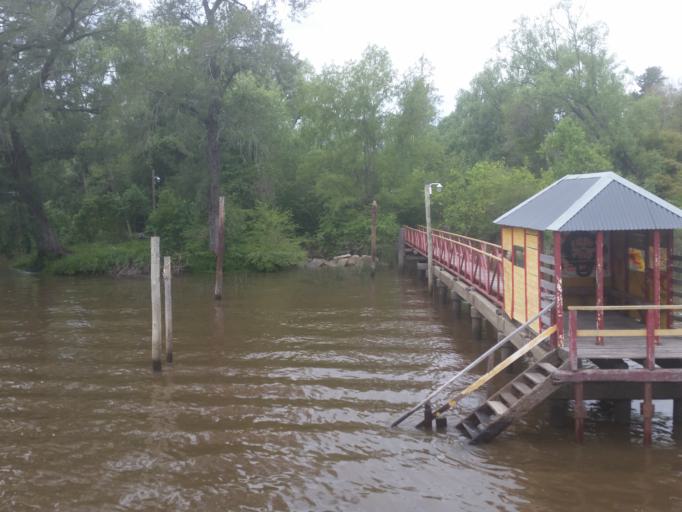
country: AR
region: Buenos Aires
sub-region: Partido de Tigre
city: Tigre
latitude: -34.3989
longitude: -58.5732
